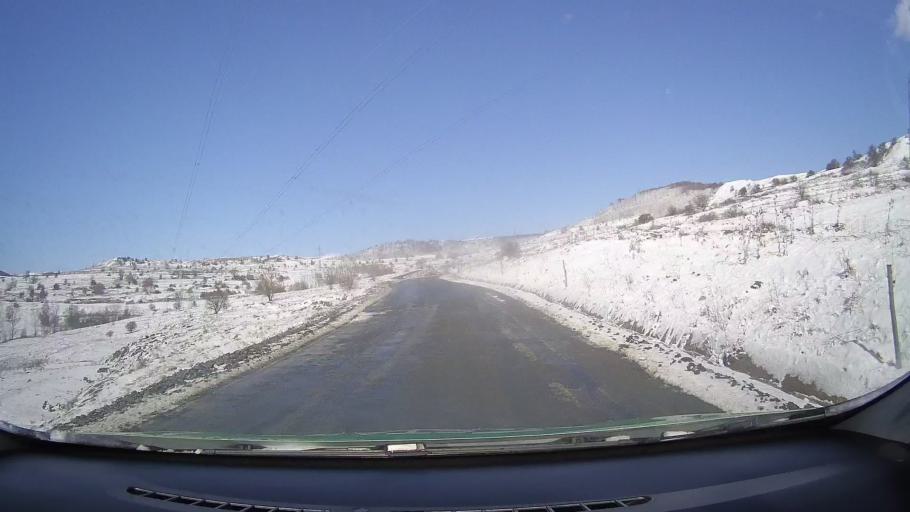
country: RO
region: Sibiu
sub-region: Comuna Avrig
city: Avrig
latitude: 45.7681
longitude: 24.3863
